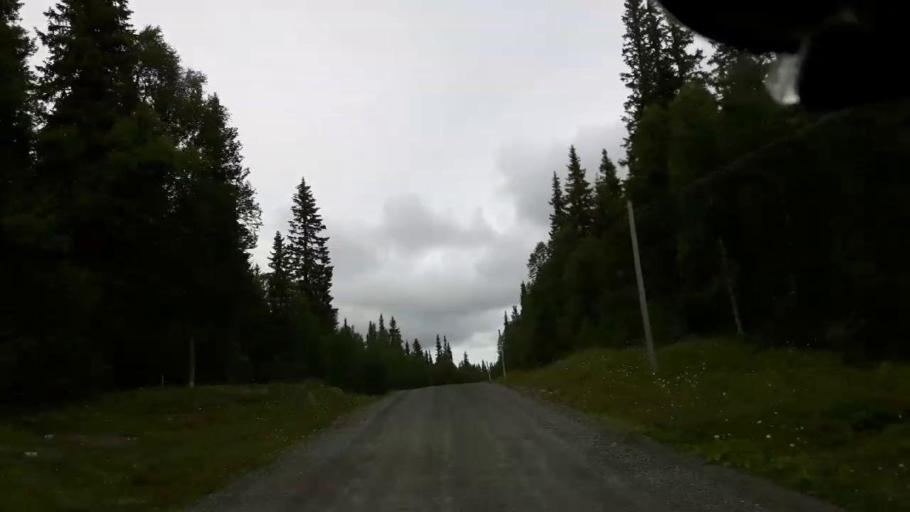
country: SE
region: Jaemtland
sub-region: Krokoms Kommun
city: Valla
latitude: 63.7514
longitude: 13.8355
